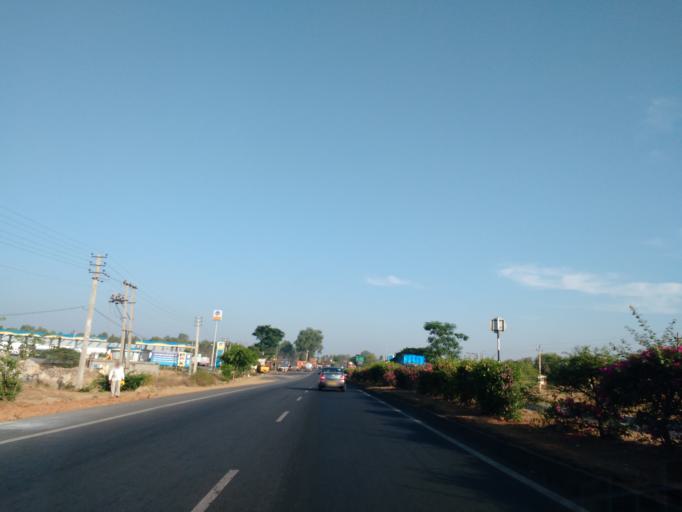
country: IN
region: Karnataka
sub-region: Bangalore Rural
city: Nelamangala
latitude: 13.1802
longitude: 77.2908
